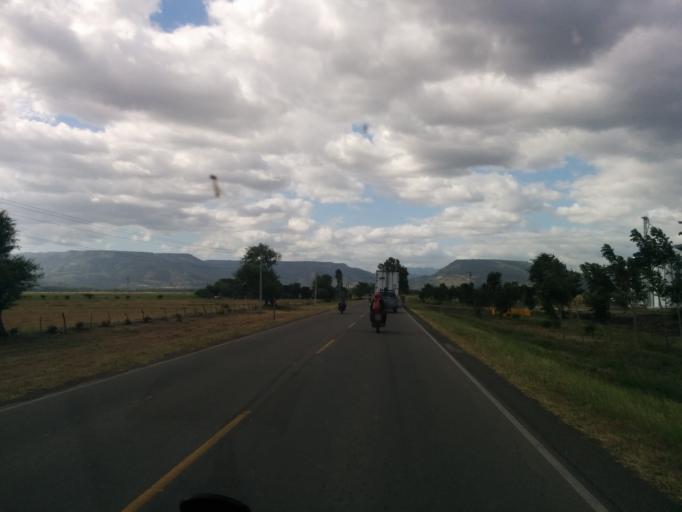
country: NI
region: Matagalpa
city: Ciudad Dario
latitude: 12.8852
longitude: -86.1478
